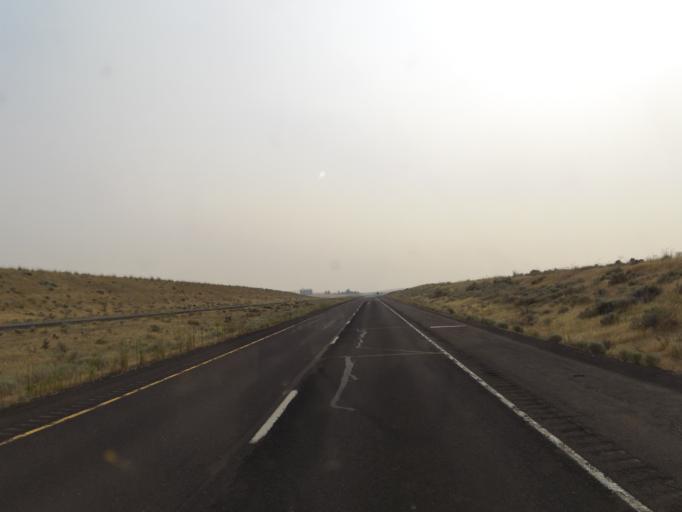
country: US
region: Washington
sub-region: Franklin County
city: Connell
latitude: 46.8071
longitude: -118.7224
